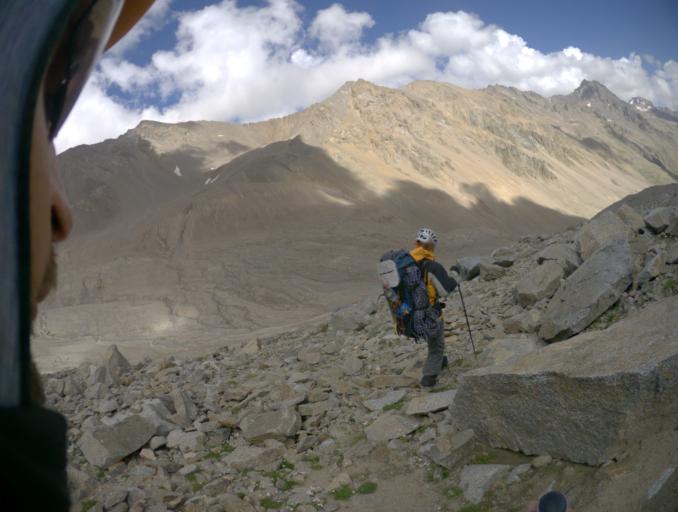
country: RU
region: Kabardino-Balkariya
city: Terskol
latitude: 43.3335
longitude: 42.5474
